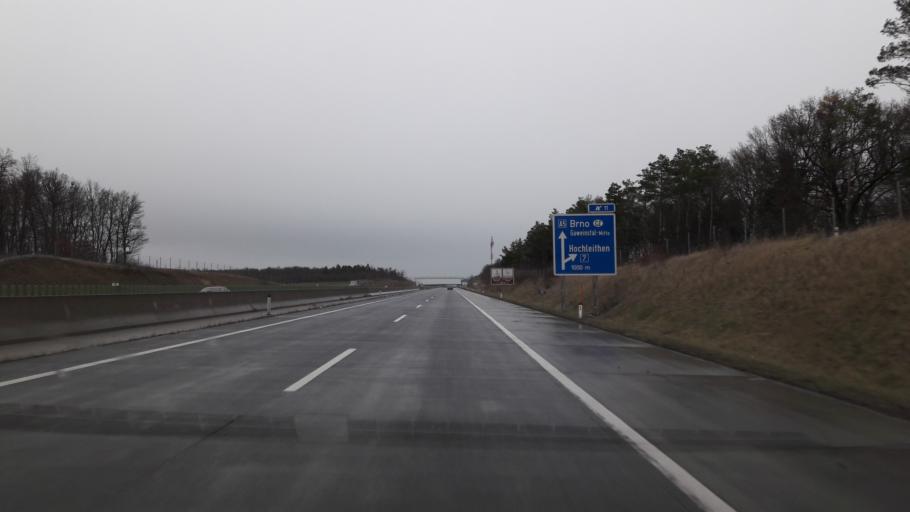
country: AT
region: Lower Austria
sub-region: Politischer Bezirk Mistelbach
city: Wolkersdorf im Weinviertel
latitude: 48.4128
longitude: 16.5391
